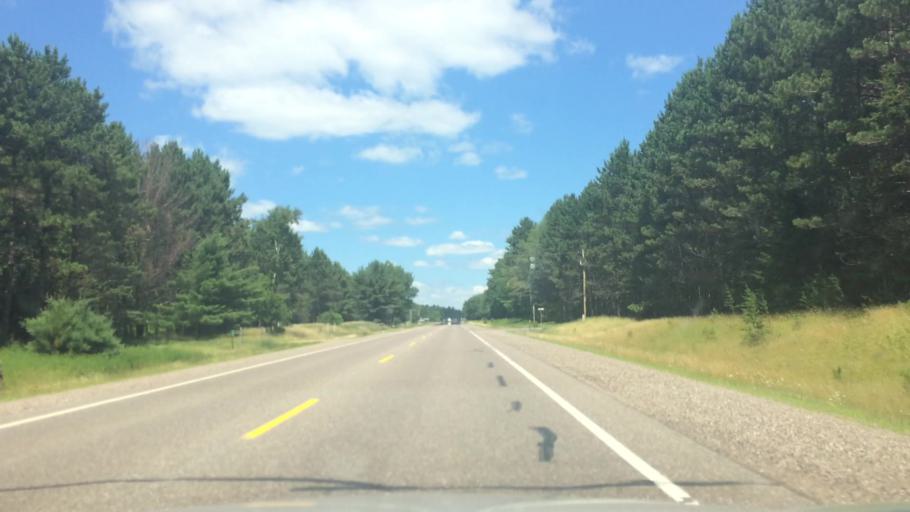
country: US
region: Wisconsin
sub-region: Vilas County
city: Lac du Flambeau
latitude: 45.9727
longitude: -89.6995
